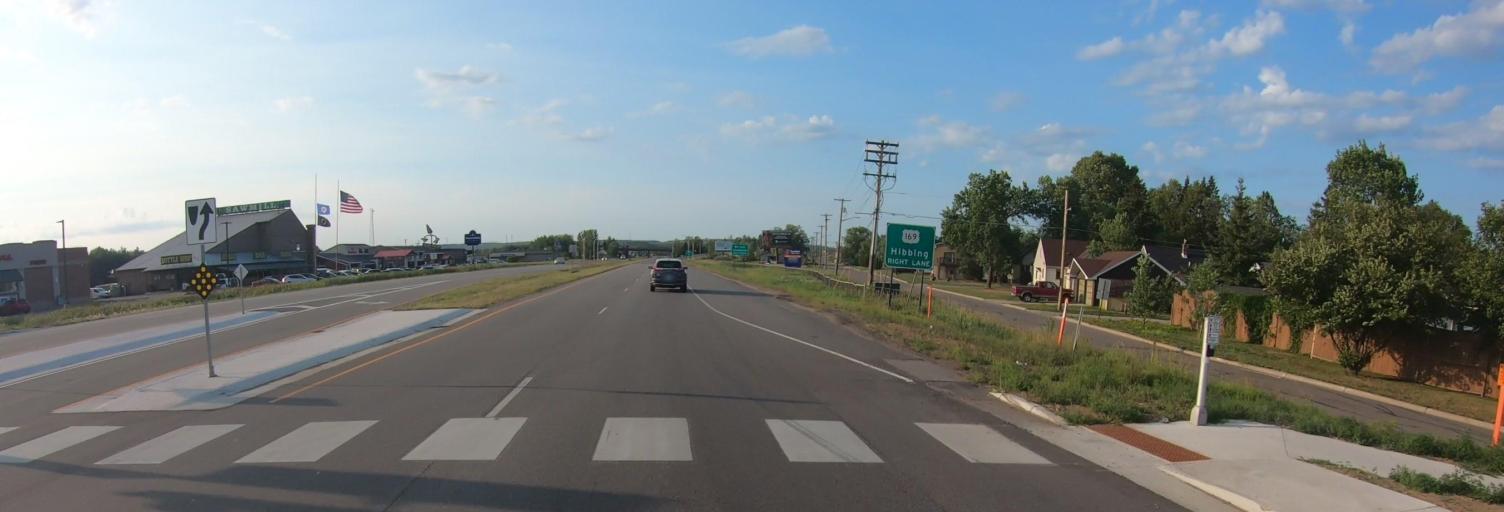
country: US
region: Minnesota
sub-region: Saint Louis County
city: Virginia
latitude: 47.5132
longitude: -92.5595
